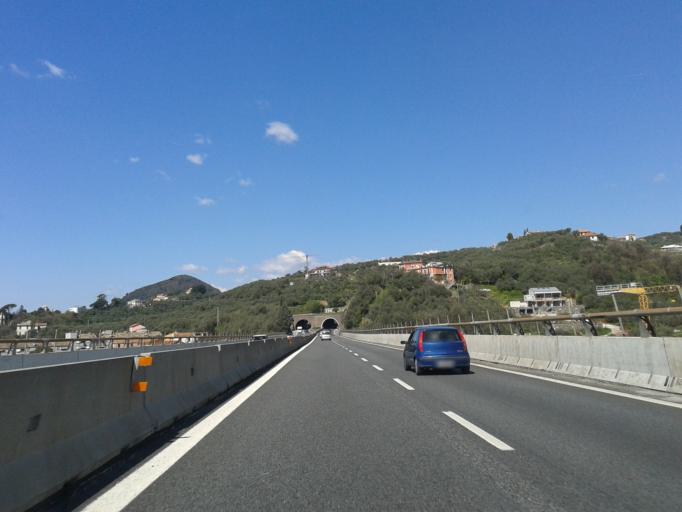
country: IT
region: Liguria
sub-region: Provincia di Genova
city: San Salvatore
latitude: 44.3202
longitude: 9.3432
